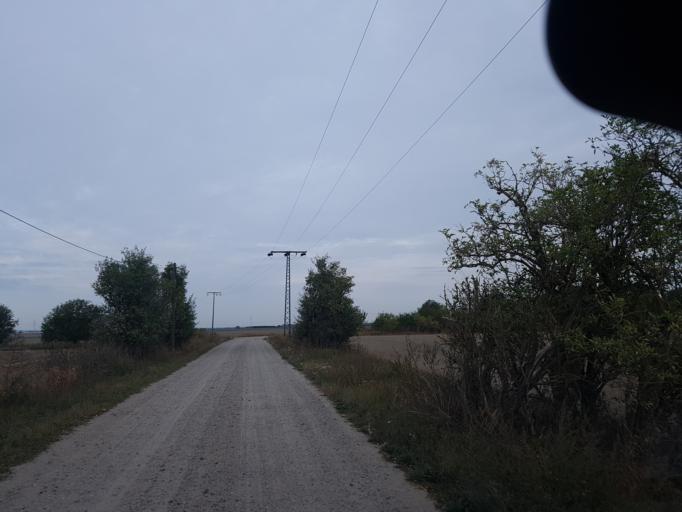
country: DE
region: Saxony-Anhalt
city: Kropstadt
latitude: 52.0049
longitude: 12.8211
